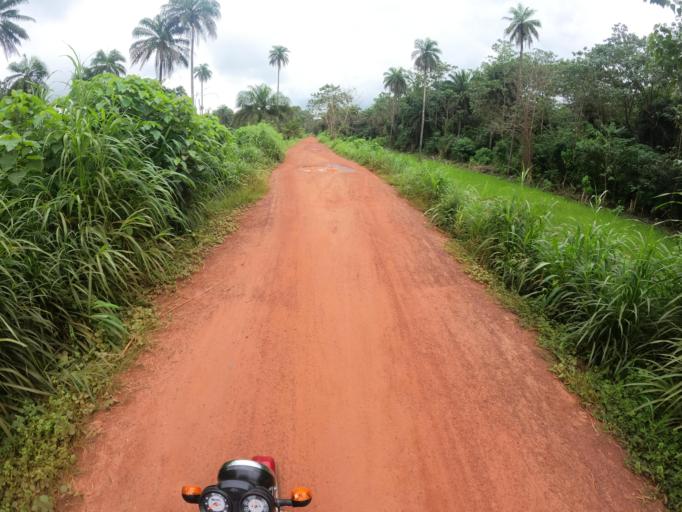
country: SL
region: Northern Province
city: Kamakwie
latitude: 9.5078
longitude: -12.2635
